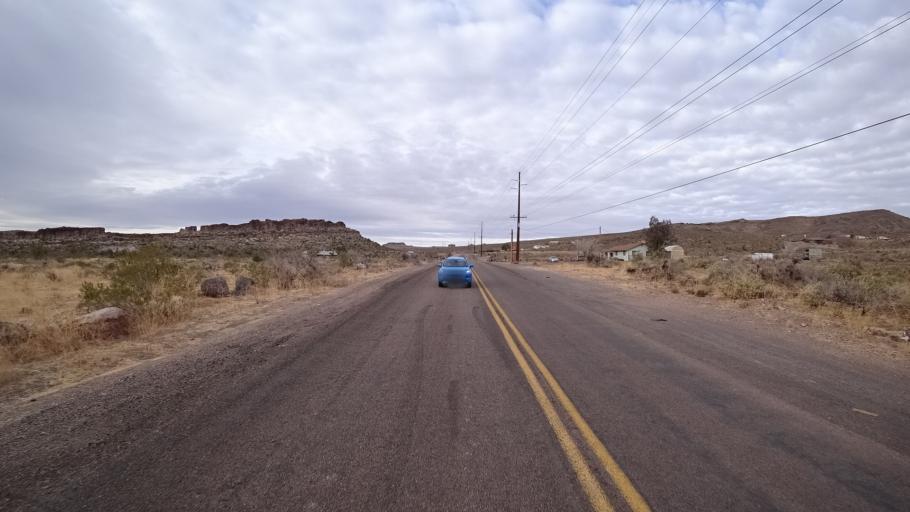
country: US
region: Arizona
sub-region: Mohave County
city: Kingman
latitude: 35.2164
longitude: -114.0730
